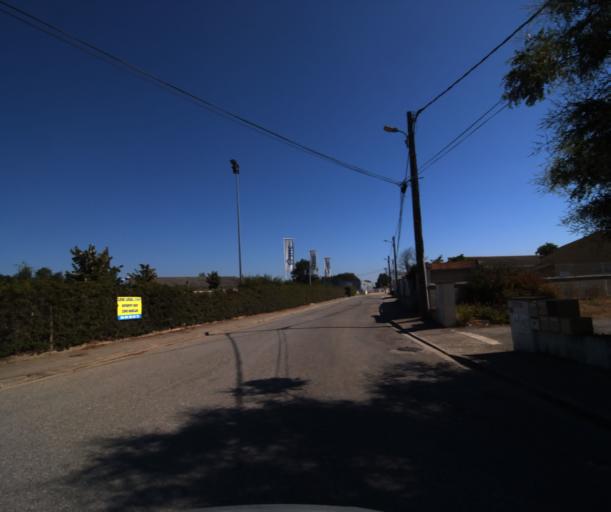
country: FR
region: Midi-Pyrenees
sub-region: Departement de la Haute-Garonne
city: Saubens
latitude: 43.4841
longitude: 1.3348
